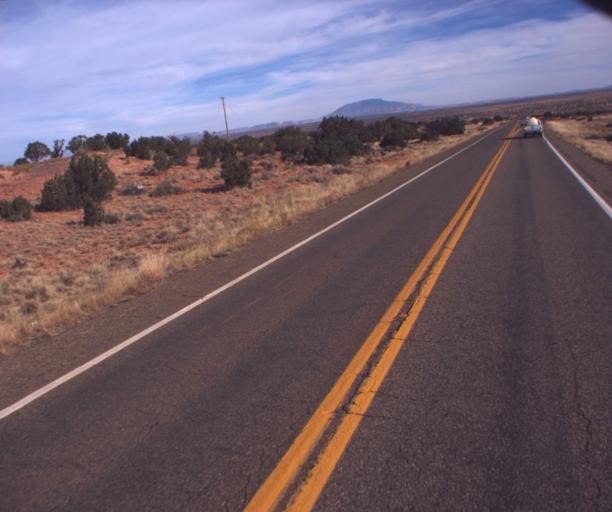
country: US
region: Arizona
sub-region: Coconino County
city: Kaibito
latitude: 36.5931
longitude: -111.0977
